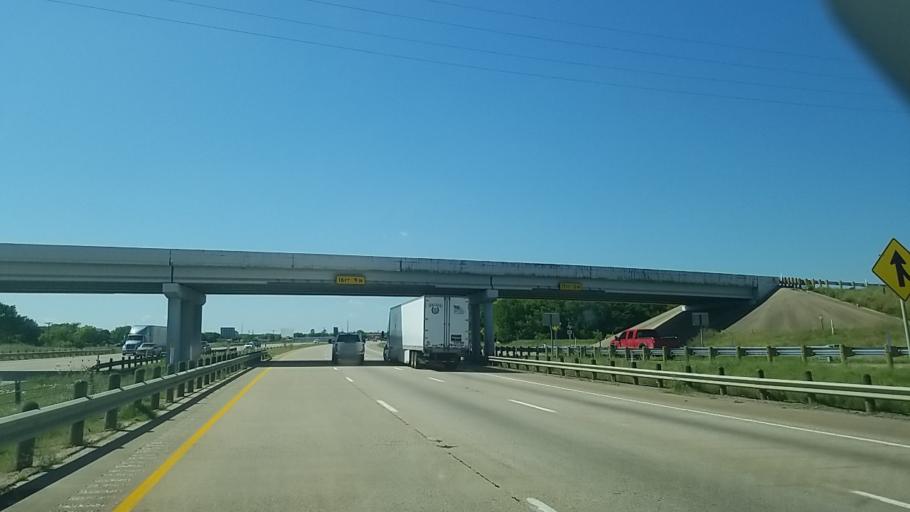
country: US
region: Texas
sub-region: Ellis County
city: Ennis
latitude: 32.3744
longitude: -96.6447
